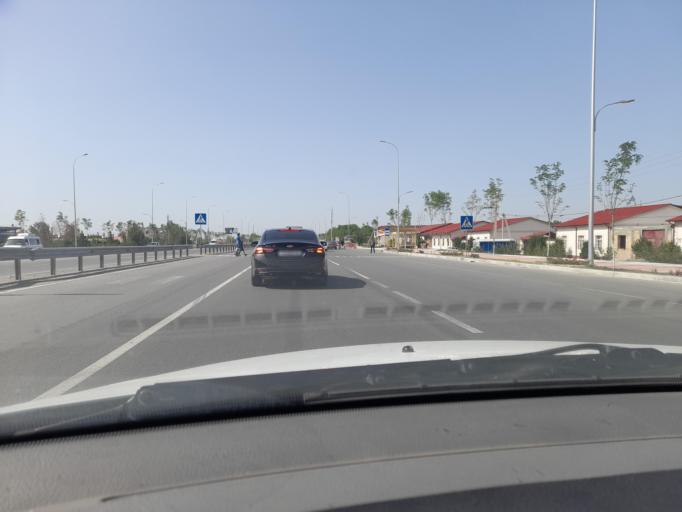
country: UZ
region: Samarqand
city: Daxbet
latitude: 39.7187
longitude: 66.9487
